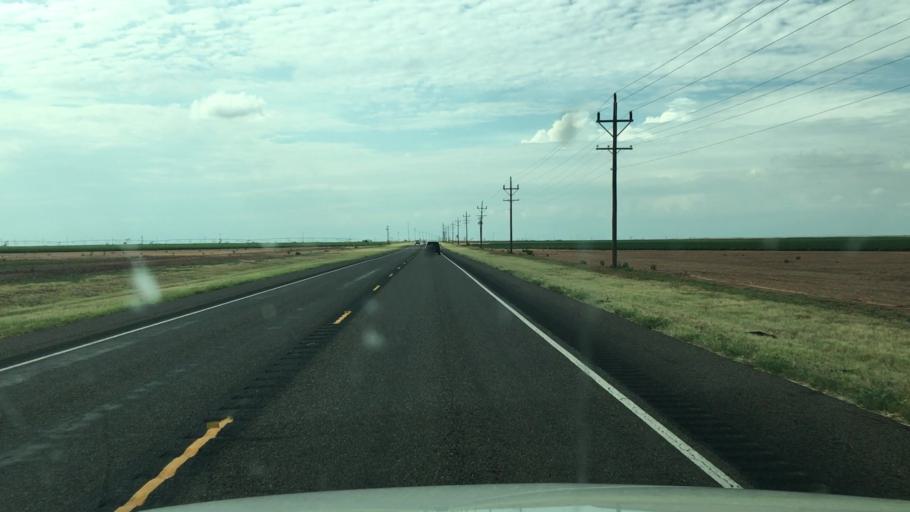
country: US
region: Texas
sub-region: Dawson County
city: Lamesa
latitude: 32.8841
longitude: -102.0839
